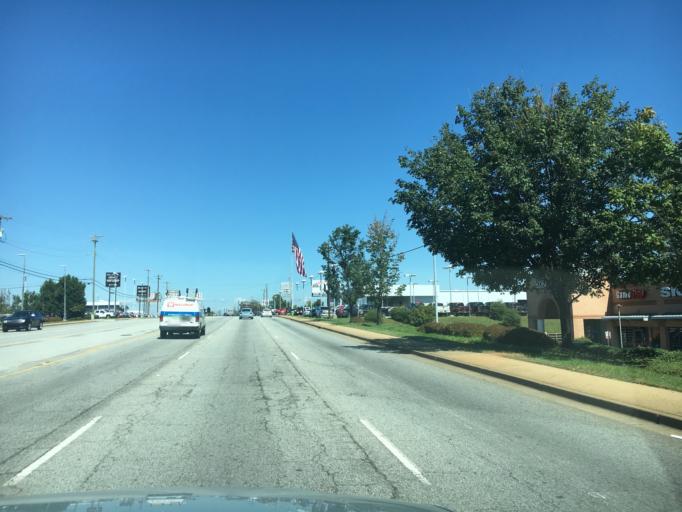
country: US
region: South Carolina
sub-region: Greenville County
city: Mauldin
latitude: 34.8209
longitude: -82.3417
